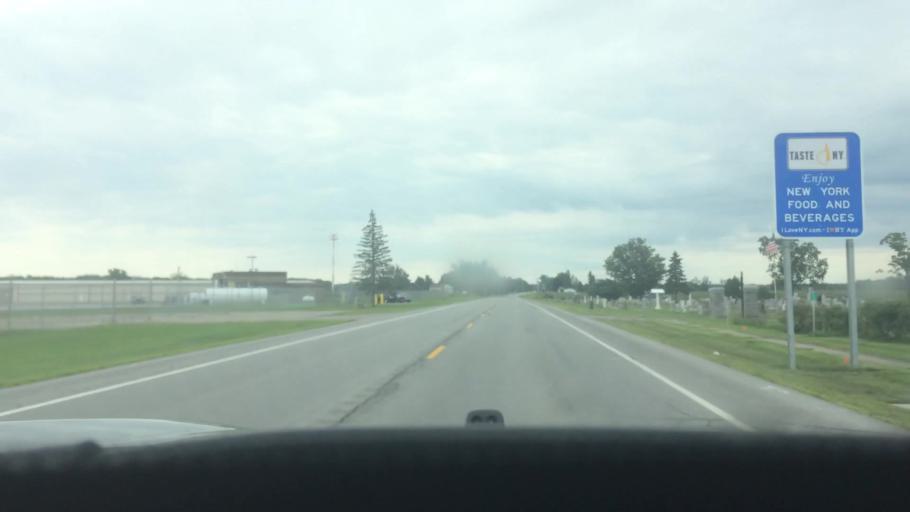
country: US
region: New York
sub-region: St. Lawrence County
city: Ogdensburg
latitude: 44.6789
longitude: -75.4779
